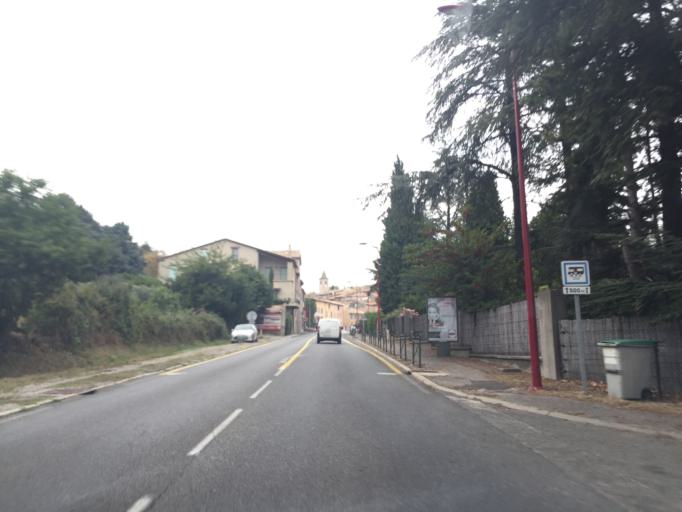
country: FR
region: Provence-Alpes-Cote d'Azur
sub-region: Departement des Alpes-de-Haute-Provence
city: Volonne
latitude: 44.0910
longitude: 6.0098
